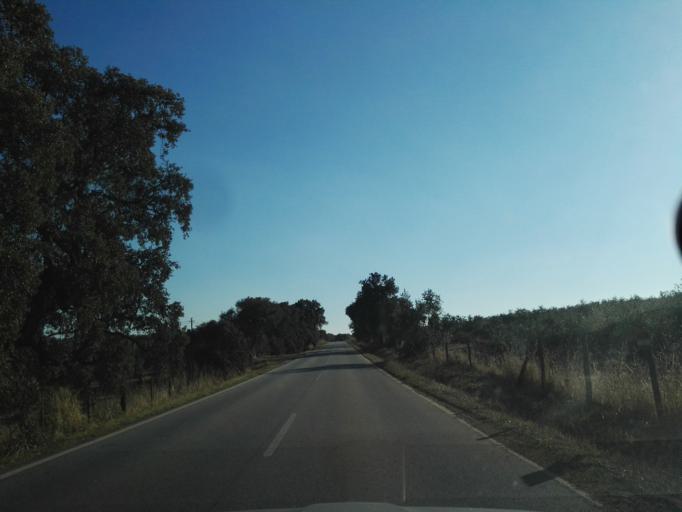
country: PT
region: Portalegre
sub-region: Elvas
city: Elvas
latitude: 38.9183
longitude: -7.1820
